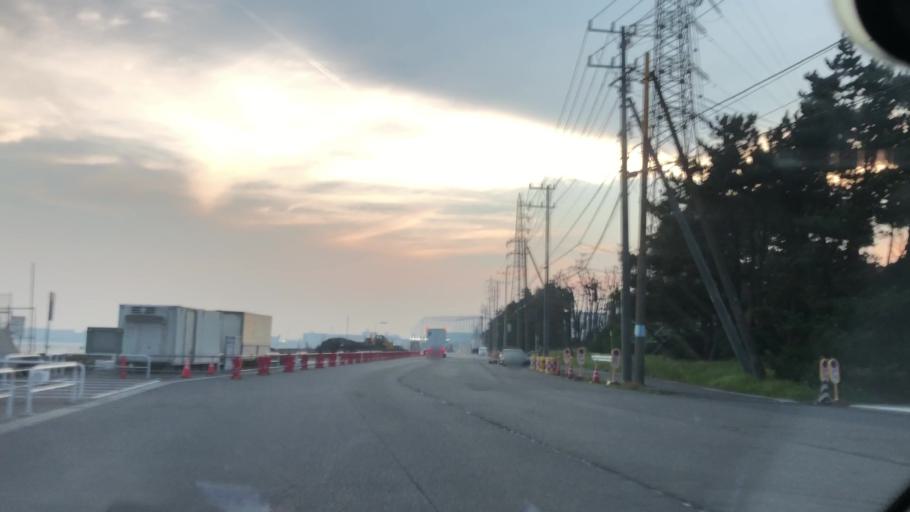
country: JP
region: Chiba
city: Funabashi
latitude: 35.6679
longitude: 139.9412
